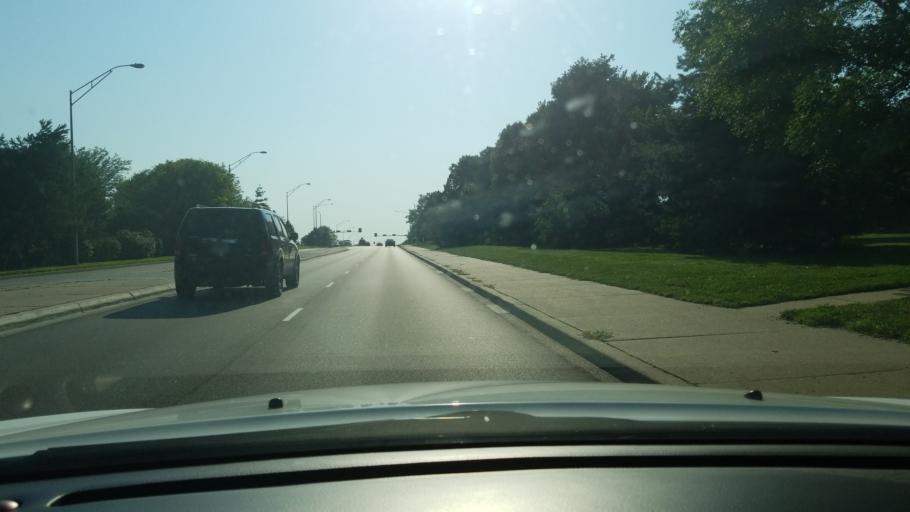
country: US
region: Nebraska
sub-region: Lancaster County
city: Lincoln
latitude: 40.7554
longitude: -96.6605
